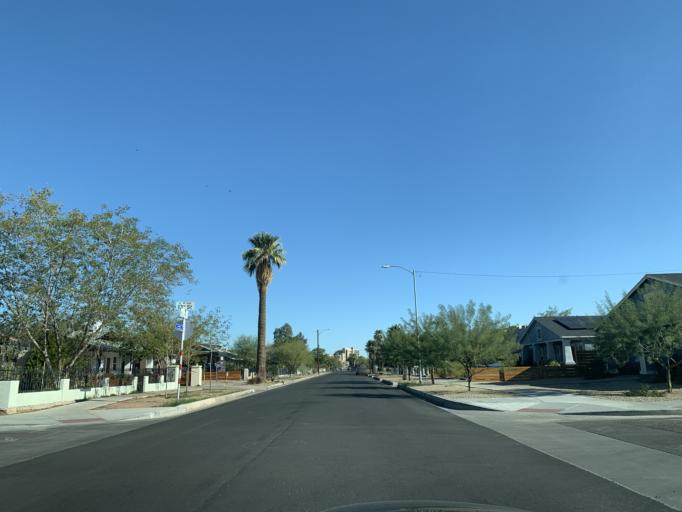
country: US
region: Arizona
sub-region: Maricopa County
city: Phoenix
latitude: 33.4548
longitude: -112.0545
